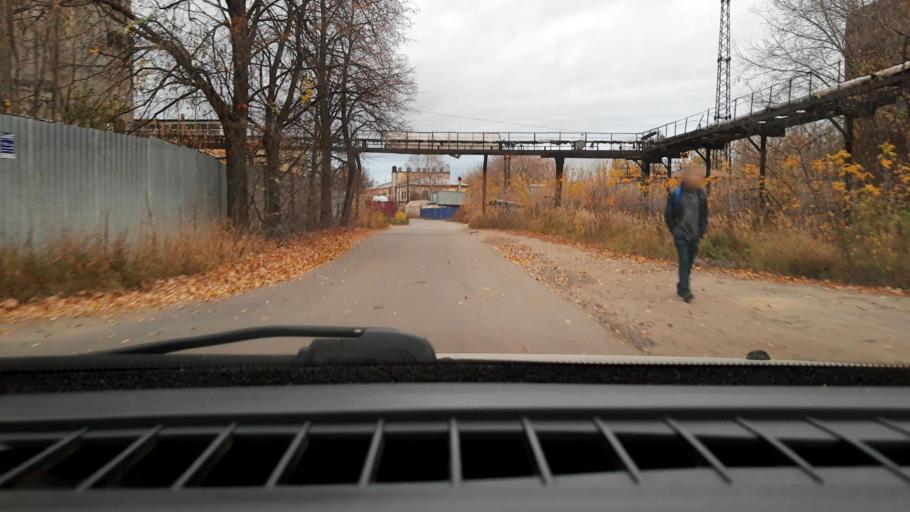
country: RU
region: Nizjnij Novgorod
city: Nizhniy Novgorod
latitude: 56.3355
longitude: 43.8926
